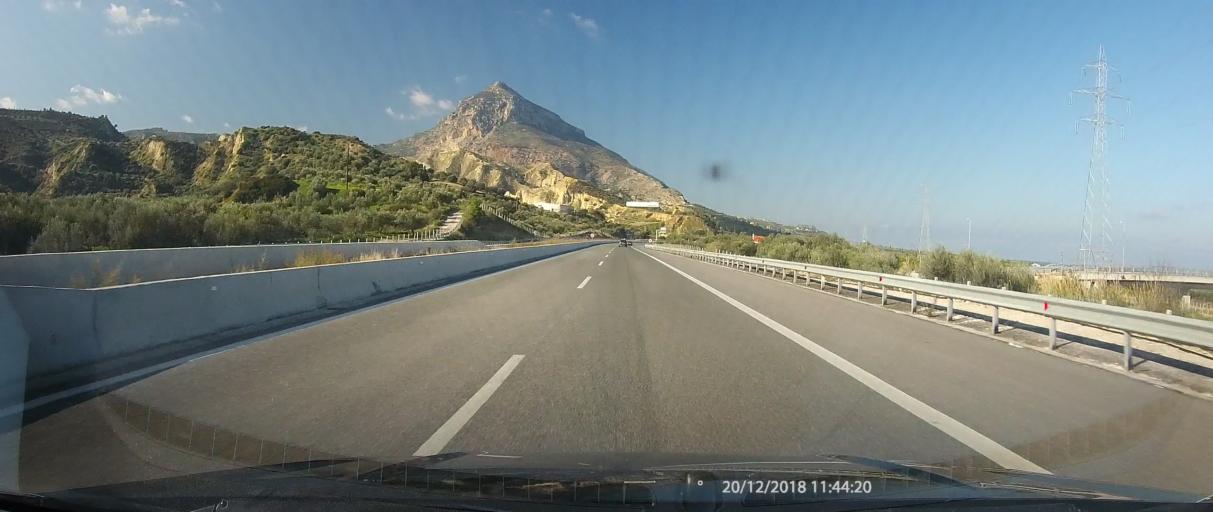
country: GR
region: Peloponnese
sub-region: Nomos Korinthias
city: Xylokastro
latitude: 38.0784
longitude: 22.6030
